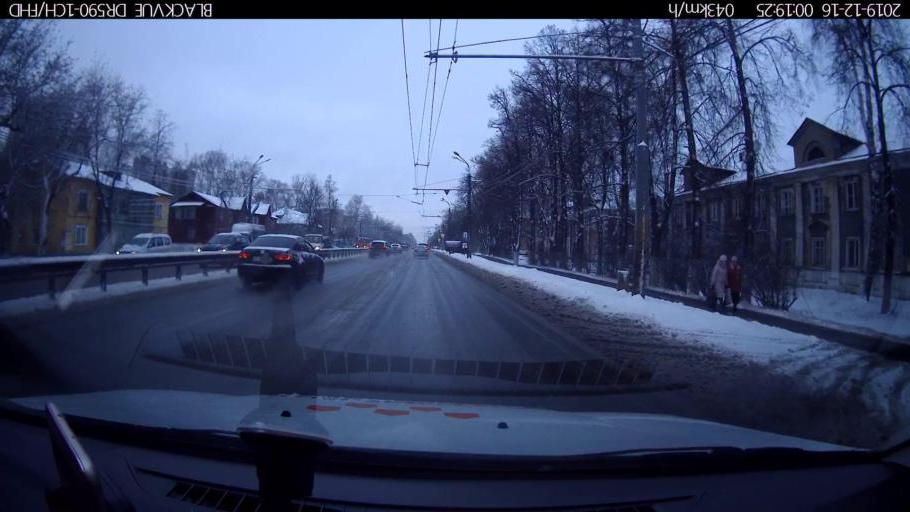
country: RU
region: Nizjnij Novgorod
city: Nizhniy Novgorod
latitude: 56.3165
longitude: 43.8963
